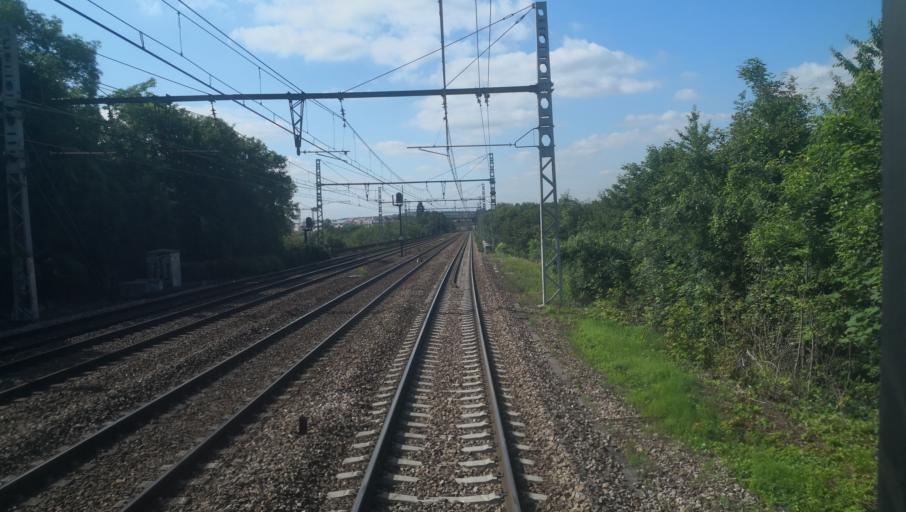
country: FR
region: Ile-de-France
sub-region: Departement de l'Essonne
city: Epinay-sous-Senart
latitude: 48.6935
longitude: 2.5120
